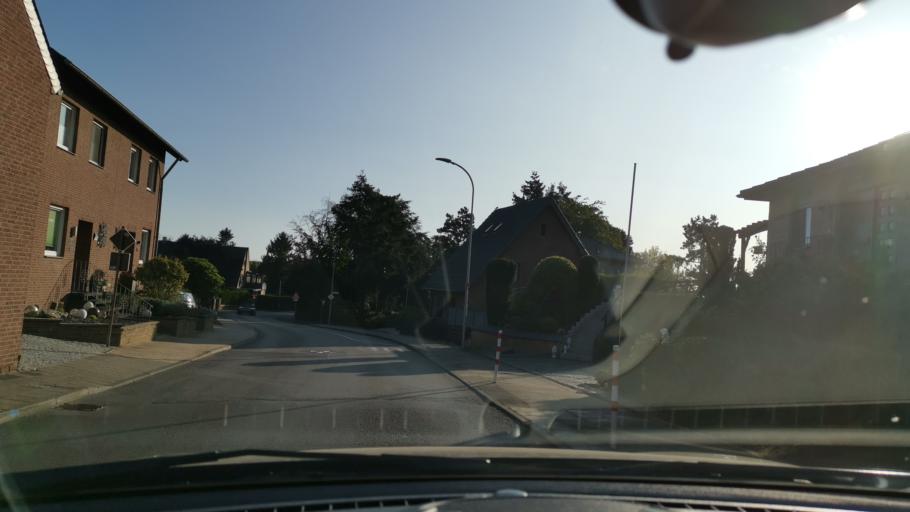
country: DE
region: North Rhine-Westphalia
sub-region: Regierungsbezirk Dusseldorf
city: Rommerskirchen
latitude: 51.1071
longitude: 6.7181
